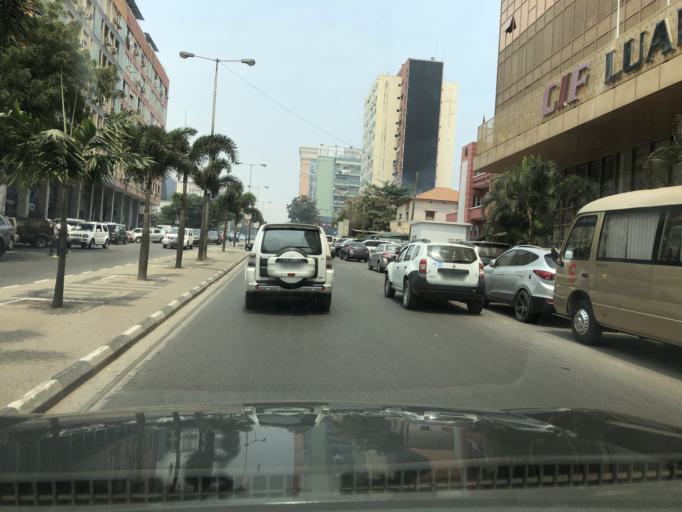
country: AO
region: Luanda
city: Luanda
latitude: -8.8177
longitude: 13.2293
